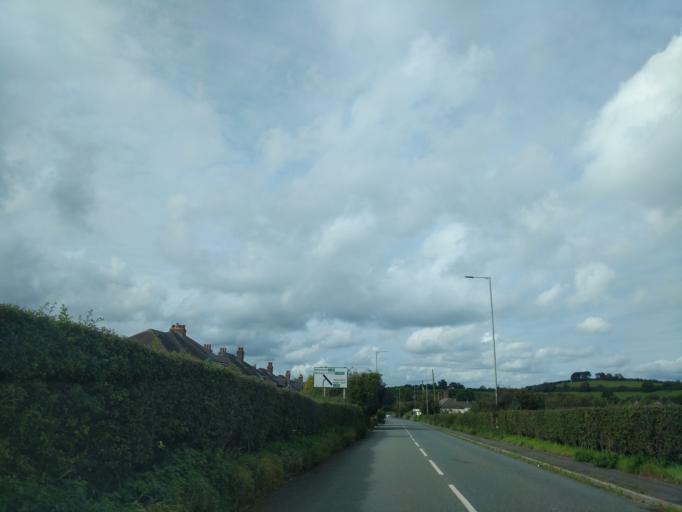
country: GB
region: England
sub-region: Staffordshire
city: Audley
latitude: 53.0076
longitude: -2.2943
